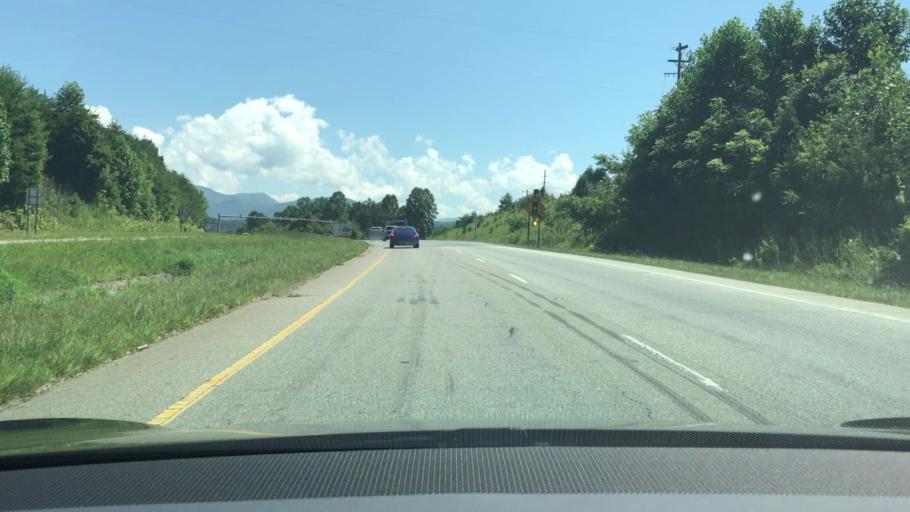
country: US
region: North Carolina
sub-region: Macon County
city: Franklin
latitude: 35.1646
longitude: -83.3731
